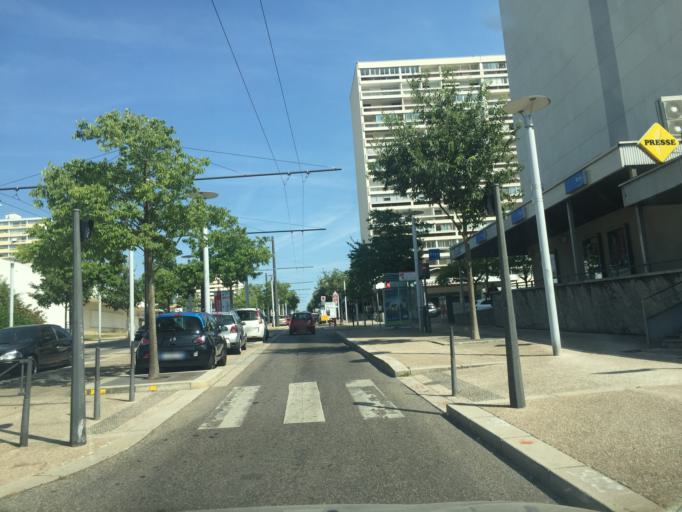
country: FR
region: Rhone-Alpes
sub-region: Departement du Rhone
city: Rillieux-la-Pape
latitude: 45.8173
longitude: 4.9010
